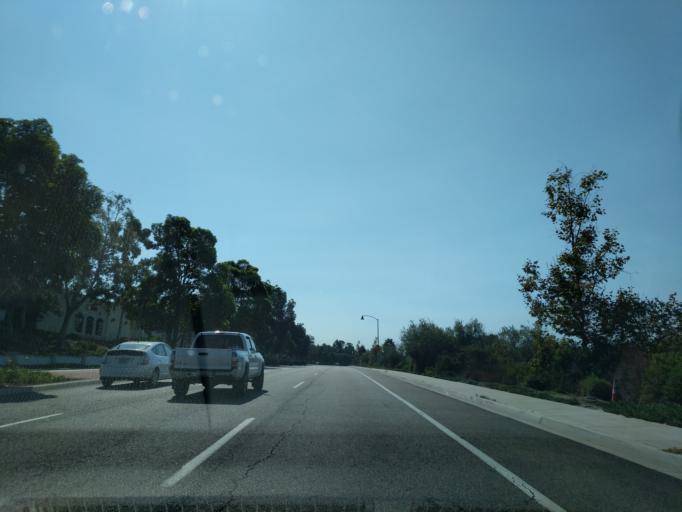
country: US
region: California
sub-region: San Diego County
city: Encinitas
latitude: 33.0839
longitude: -117.2680
